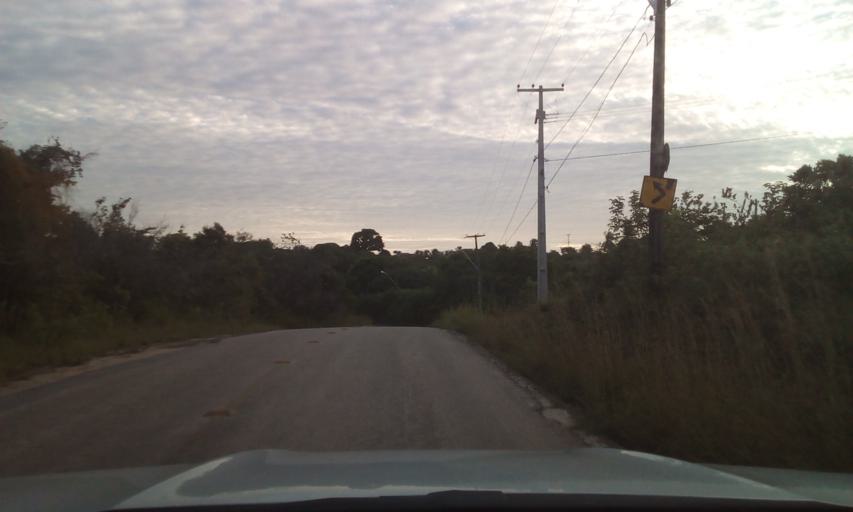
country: BR
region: Paraiba
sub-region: Conde
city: Conde
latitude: -7.2170
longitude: -34.8088
